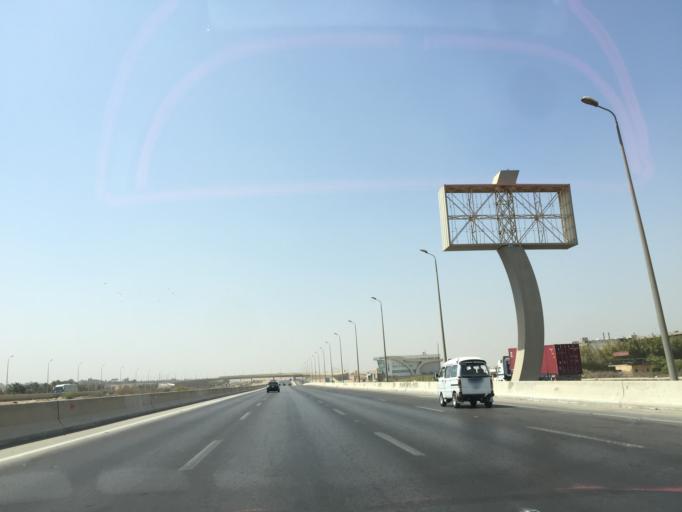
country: EG
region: Al Jizah
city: Awsim
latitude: 30.0769
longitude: 31.0027
